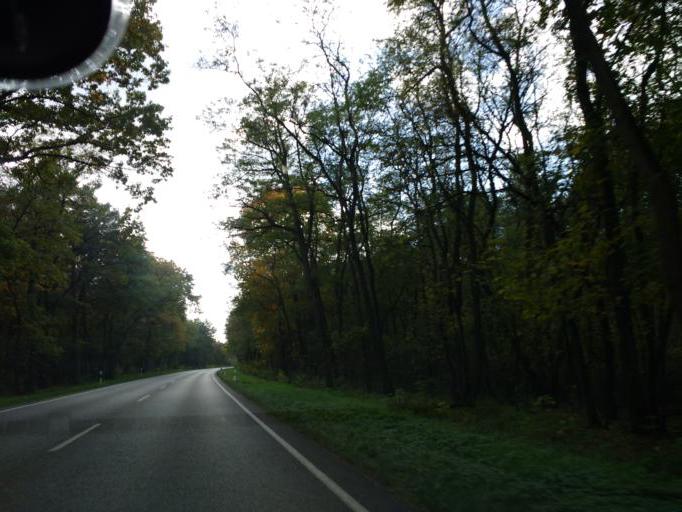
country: DE
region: Brandenburg
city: Petershagen
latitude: 52.5047
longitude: 13.7982
